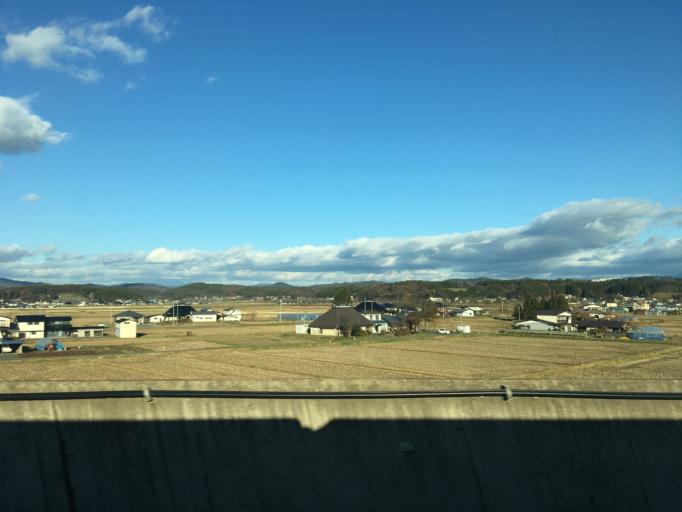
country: JP
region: Iwate
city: Mizusawa
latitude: 39.2015
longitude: 141.1507
